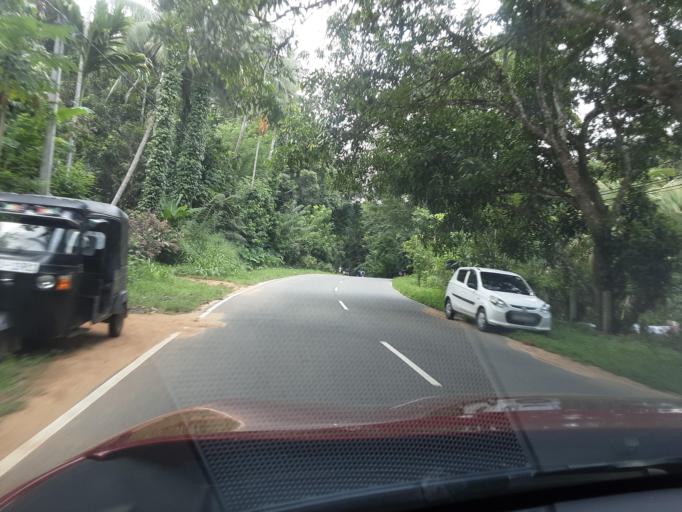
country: LK
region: Uva
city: Monaragala
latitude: 6.8965
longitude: 81.2883
